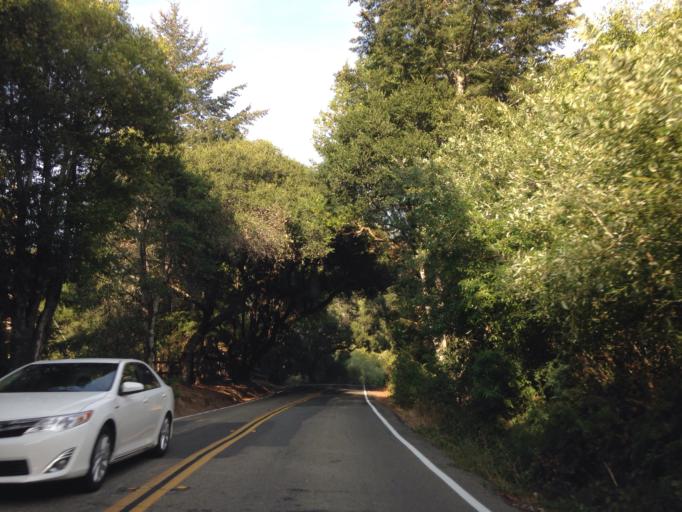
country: US
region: California
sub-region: Marin County
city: Woodacre
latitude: 38.0563
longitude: -122.6594
